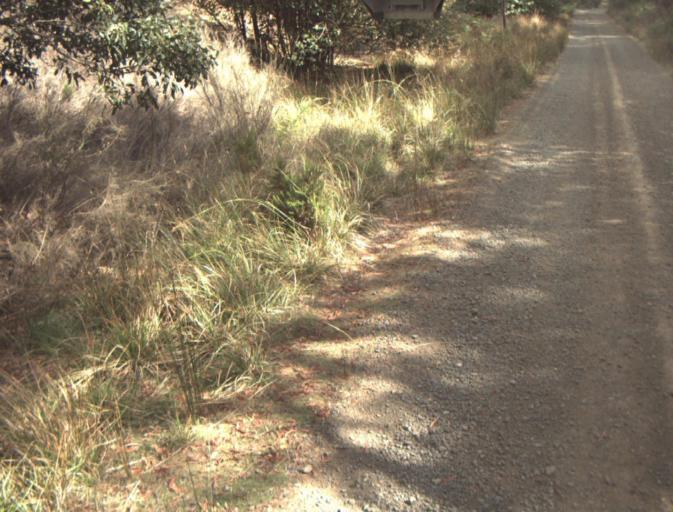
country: AU
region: Tasmania
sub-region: Launceston
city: Mayfield
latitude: -41.2812
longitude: 147.2328
